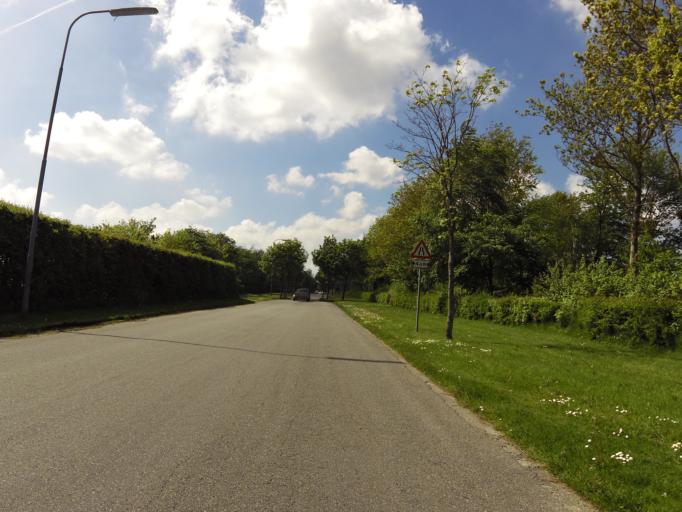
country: DK
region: South Denmark
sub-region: Tonder Kommune
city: Toftlund
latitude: 55.1829
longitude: 9.0847
